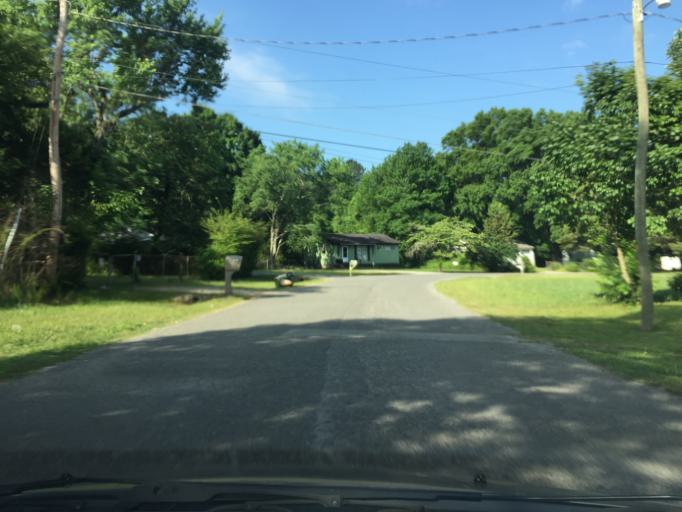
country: US
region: Tennessee
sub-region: Hamilton County
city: East Brainerd
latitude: 35.0347
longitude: -85.1879
